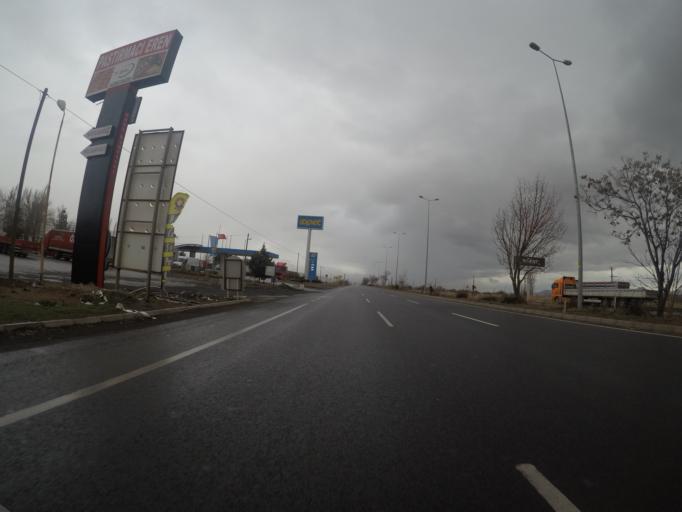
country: TR
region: Kayseri
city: Incesu
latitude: 38.6905
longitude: 35.2427
